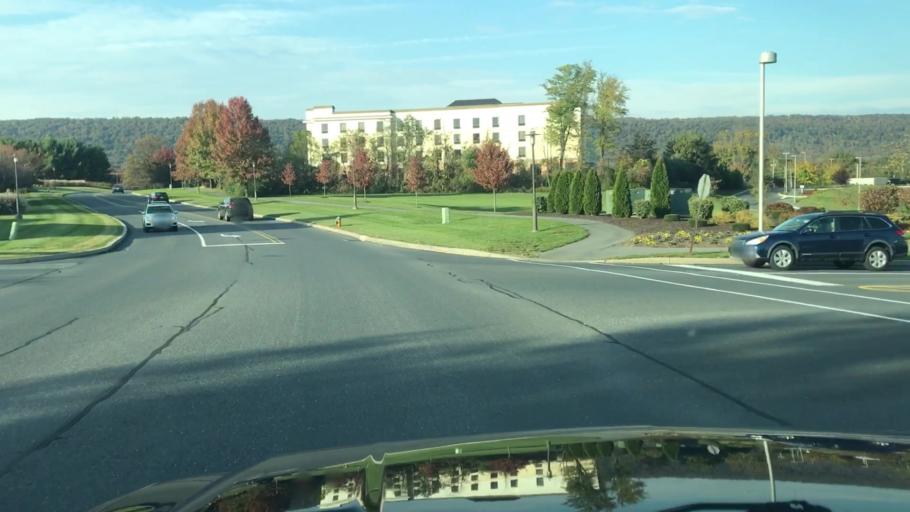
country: US
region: Pennsylvania
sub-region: Cumberland County
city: Enola
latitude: 40.2849
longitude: -76.9766
